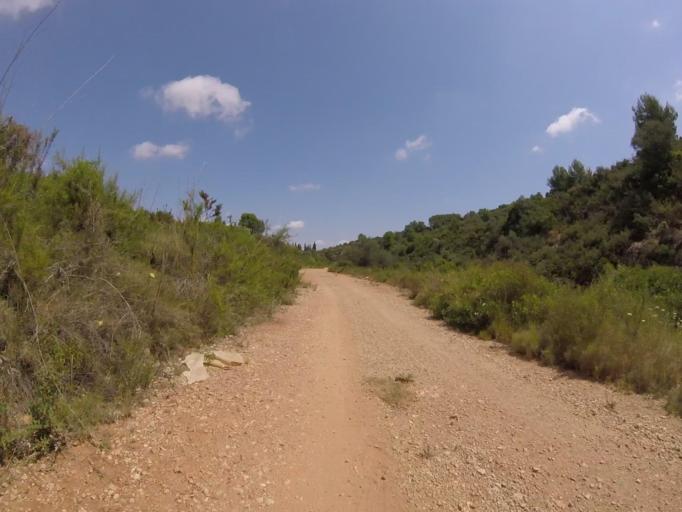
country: ES
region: Valencia
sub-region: Provincia de Castello
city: Torreblanca
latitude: 40.2077
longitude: 0.1392
